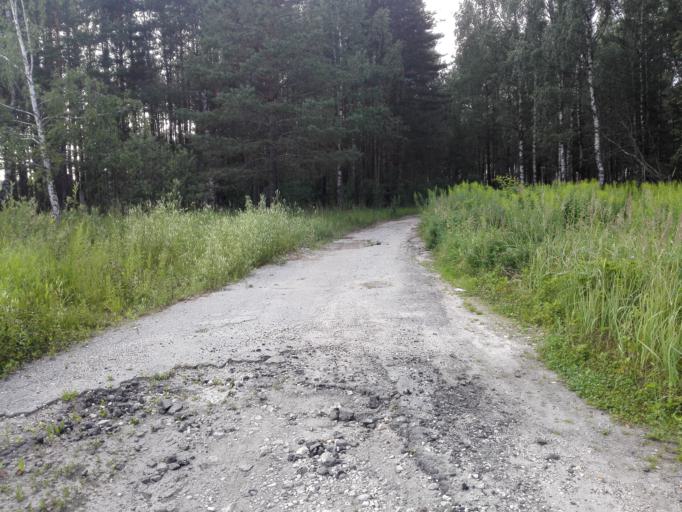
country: RU
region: Vladimir
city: Kommunar
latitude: 56.1127
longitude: 40.4613
